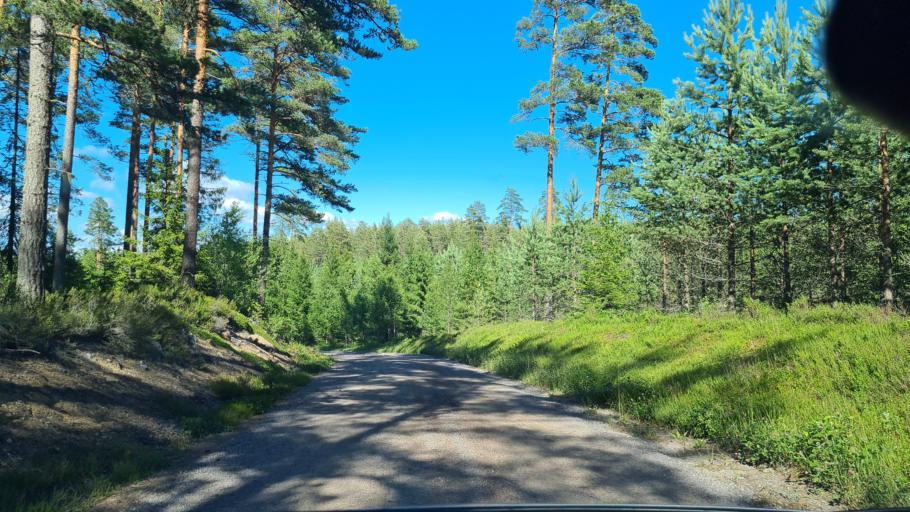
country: SE
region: OEstergoetland
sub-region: Norrkopings Kommun
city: Krokek
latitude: 58.6934
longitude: 16.4247
